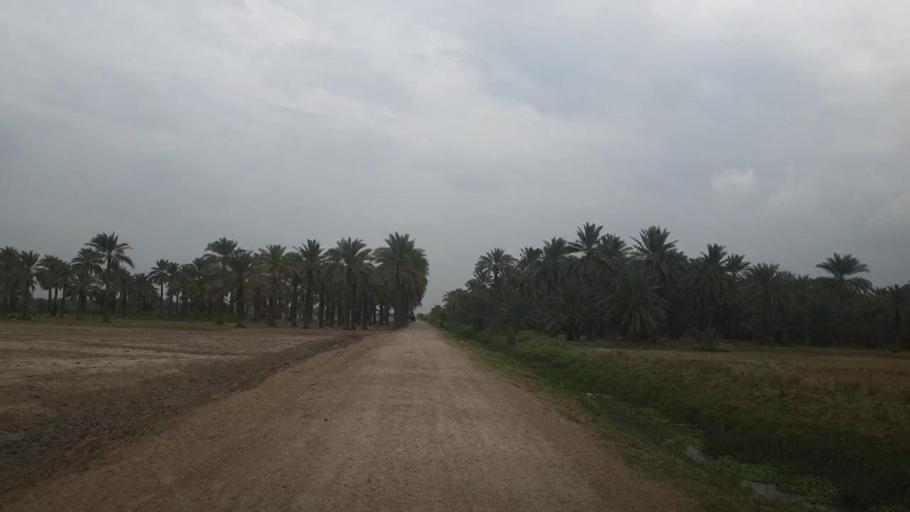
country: PK
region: Sindh
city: Khairpur
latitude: 27.5607
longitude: 68.7101
